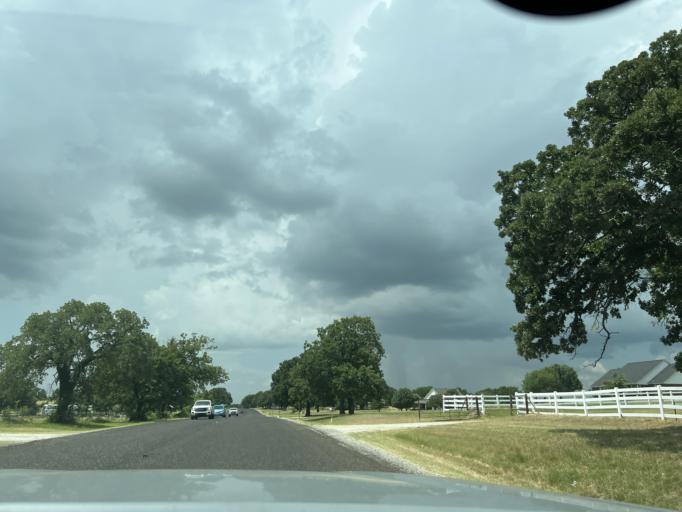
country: US
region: Texas
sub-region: Wise County
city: Decatur
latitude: 33.1900
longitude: -97.6135
